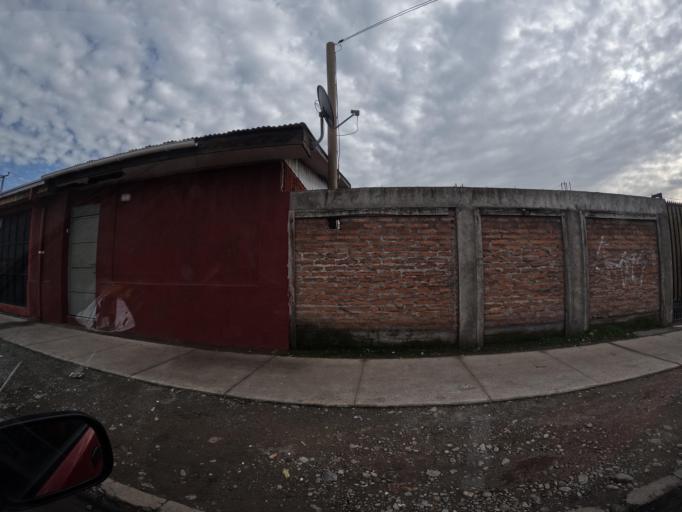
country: CL
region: Maule
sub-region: Provincia de Linares
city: Linares
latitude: -35.8547
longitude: -71.5863
